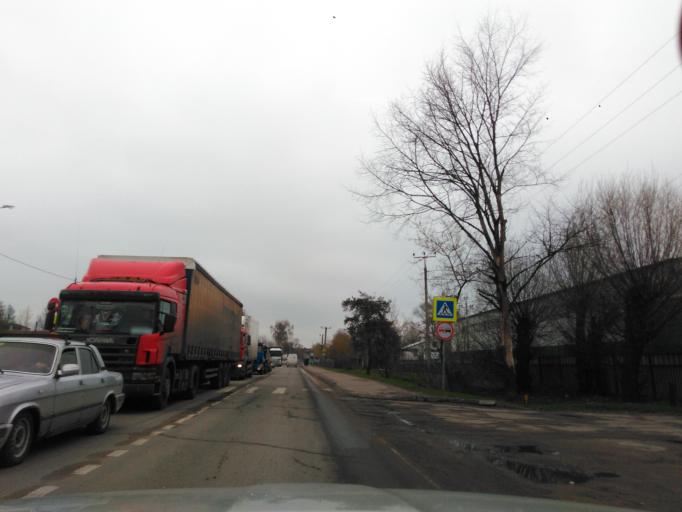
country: RU
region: Moskovskaya
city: Nakhabino
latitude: 55.8434
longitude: 37.1807
